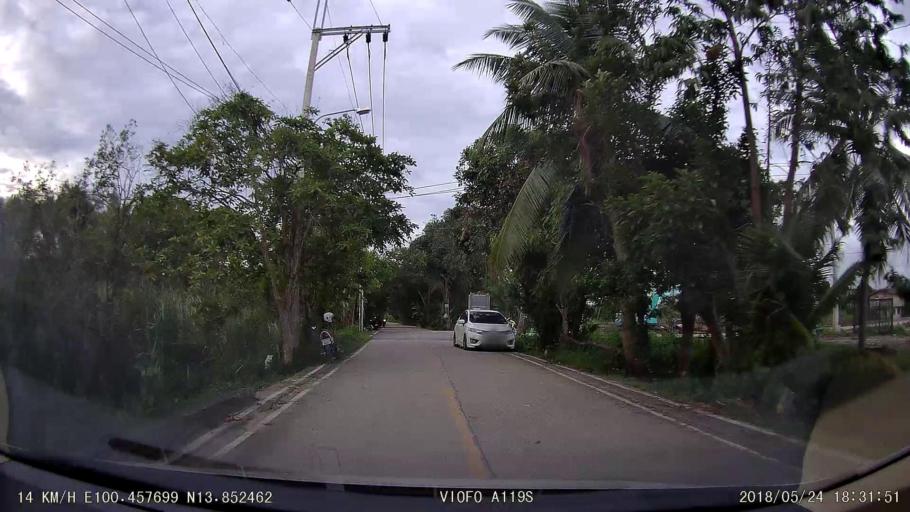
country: TH
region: Nonthaburi
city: Bang Kruai
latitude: 13.8527
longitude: 100.4575
